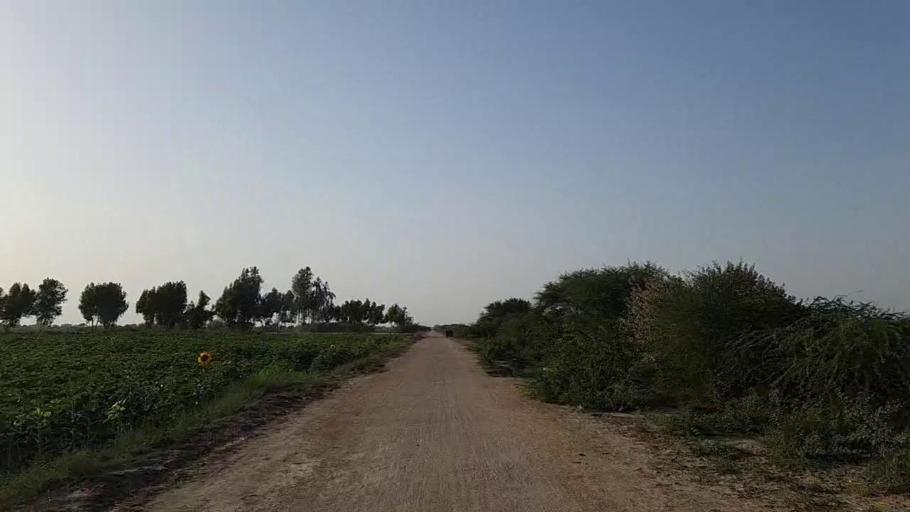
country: PK
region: Sindh
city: Jati
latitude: 24.3293
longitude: 68.1601
